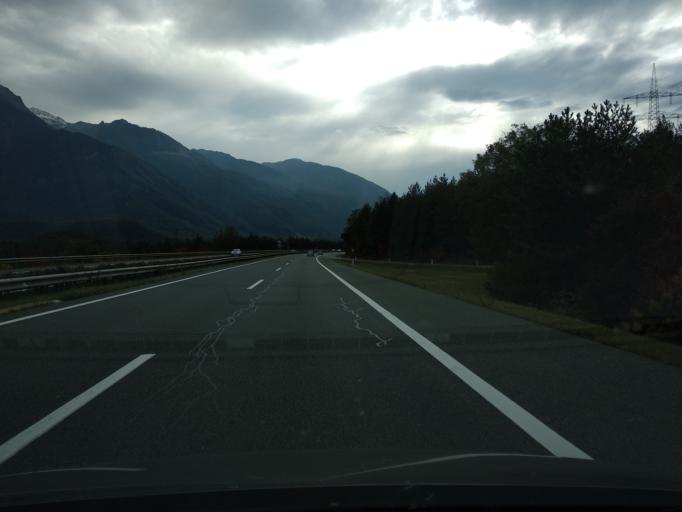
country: AT
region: Tyrol
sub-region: Politischer Bezirk Imst
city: Roppen
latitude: 47.2388
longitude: 10.8454
